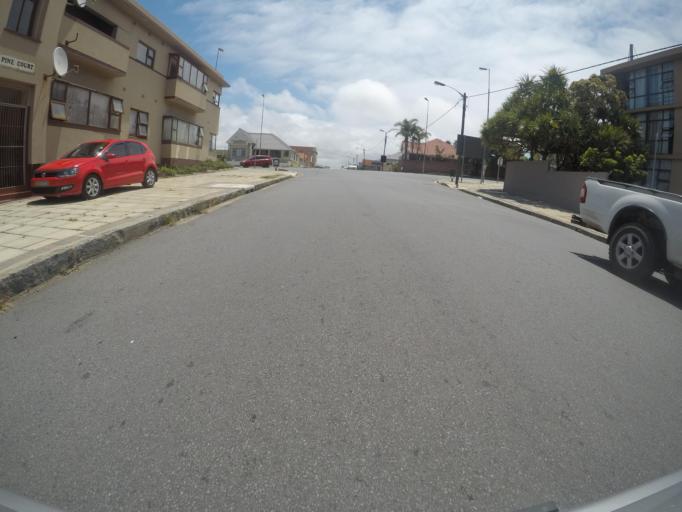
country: ZA
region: Eastern Cape
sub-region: Buffalo City Metropolitan Municipality
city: East London
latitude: -33.0171
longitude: 27.9166
